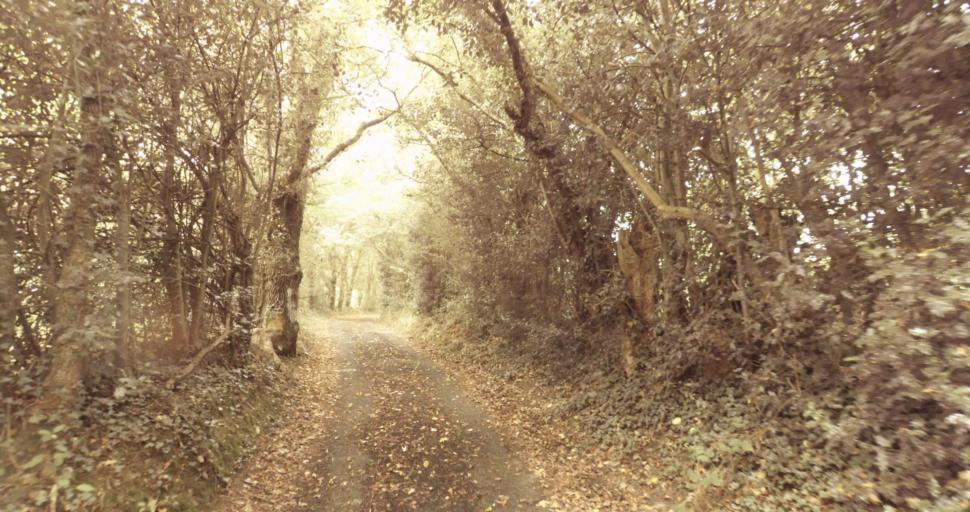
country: FR
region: Lower Normandy
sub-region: Departement du Calvados
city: Orbec
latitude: 48.9633
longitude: 0.3841
